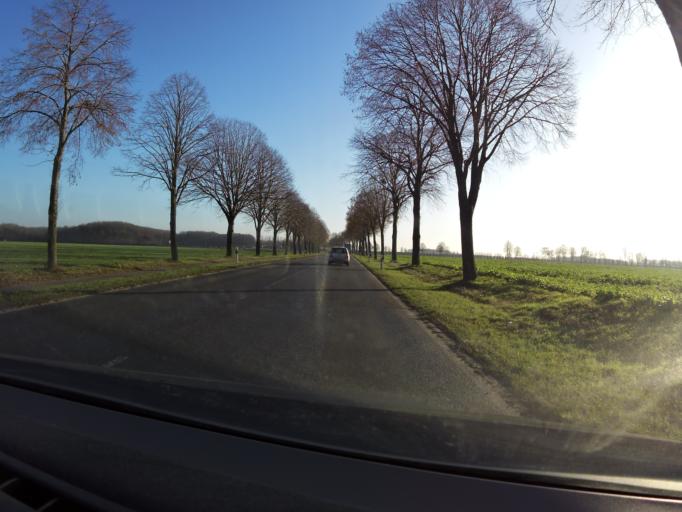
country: NL
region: Limburg
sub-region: Gemeente Venlo
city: Venlo
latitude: 51.3100
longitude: 6.2067
